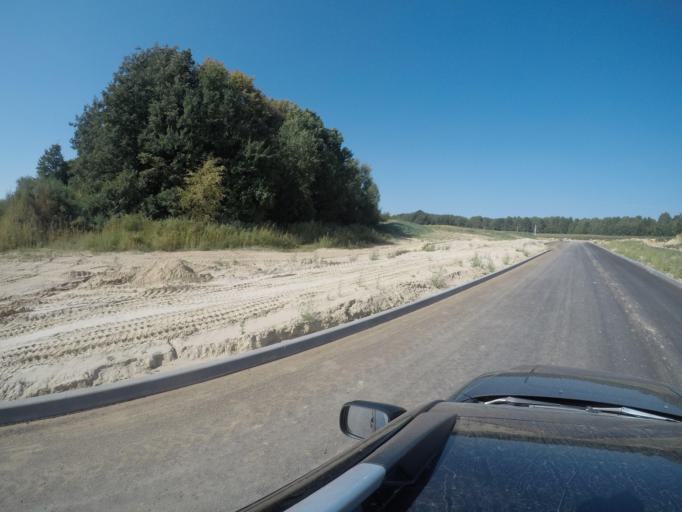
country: BY
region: Grodnenskaya
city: Hrodna
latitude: 53.7263
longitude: 23.8783
